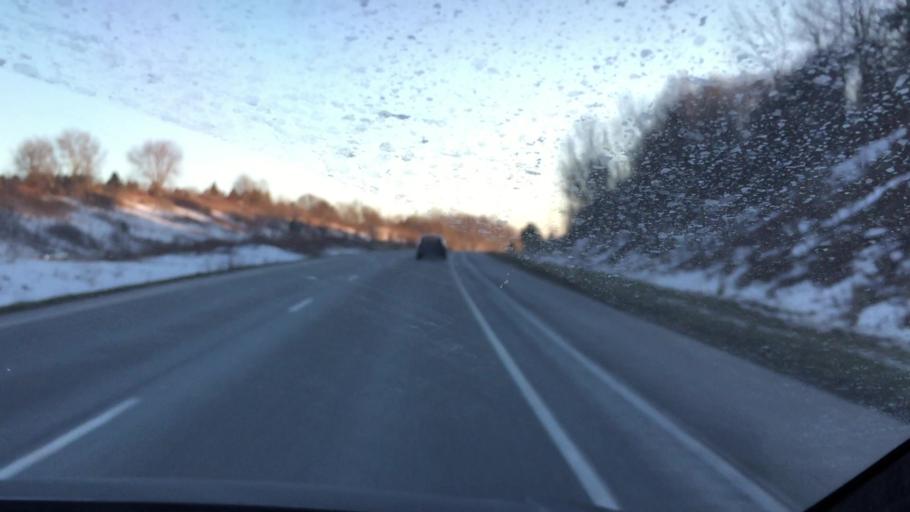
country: US
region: Pennsylvania
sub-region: Crawford County
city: Meadville
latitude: 41.6023
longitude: -80.1656
